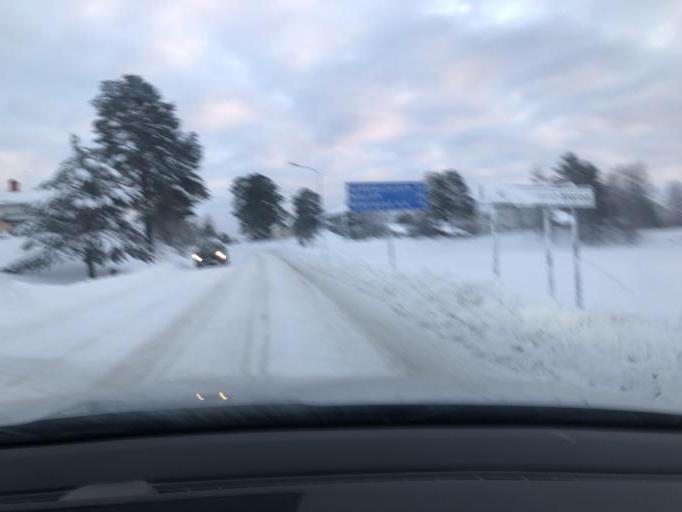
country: SE
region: Vaesternorrland
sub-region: Kramfors Kommun
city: Nordingra
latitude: 63.0093
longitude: 18.1906
